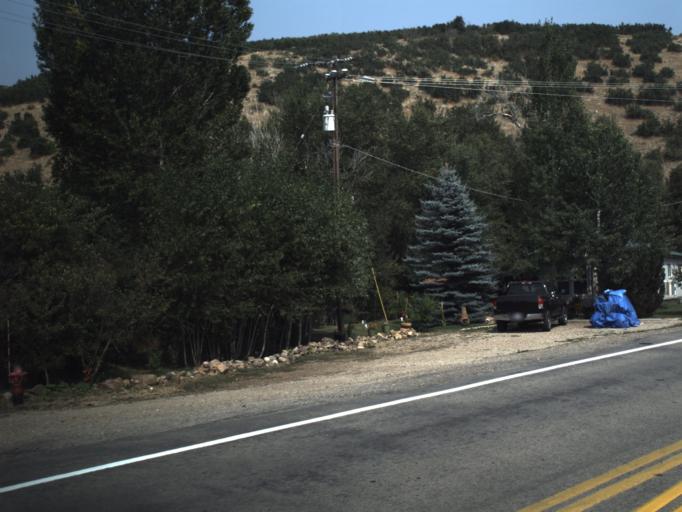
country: US
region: Utah
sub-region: Summit County
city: Kamas
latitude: 40.6431
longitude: -111.2734
